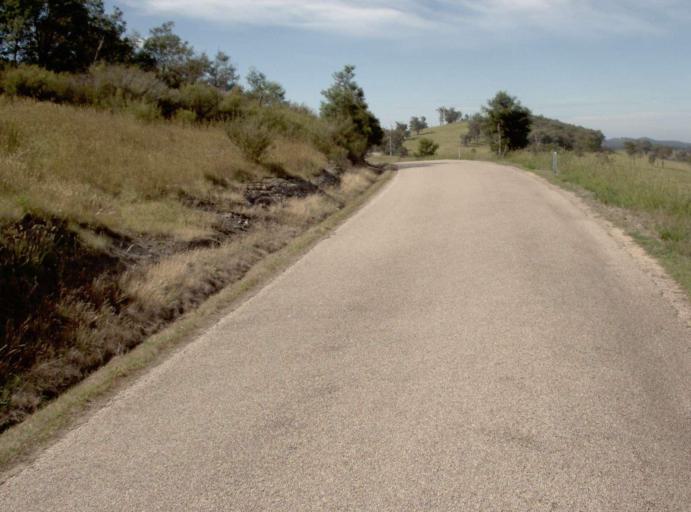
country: AU
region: Victoria
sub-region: East Gippsland
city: Lakes Entrance
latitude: -37.4979
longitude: 148.1324
